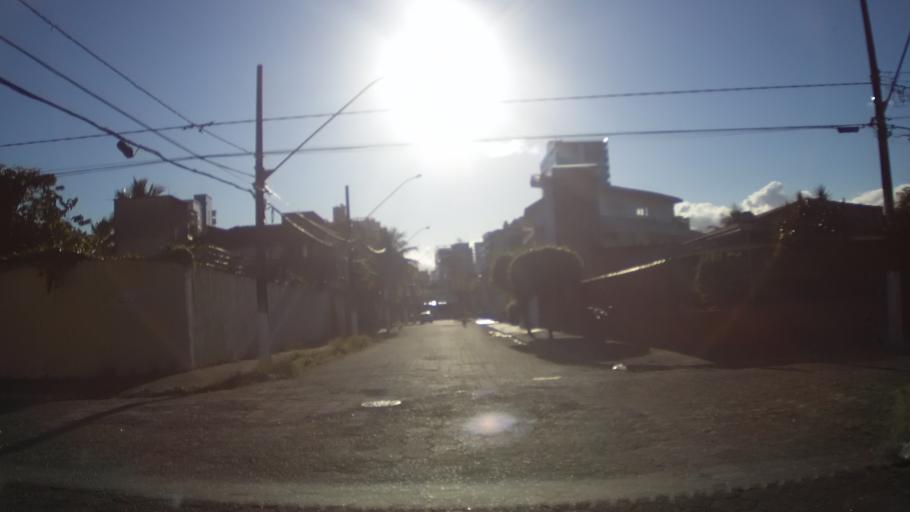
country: BR
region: Sao Paulo
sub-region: Praia Grande
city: Praia Grande
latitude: -24.0098
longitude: -46.4028
